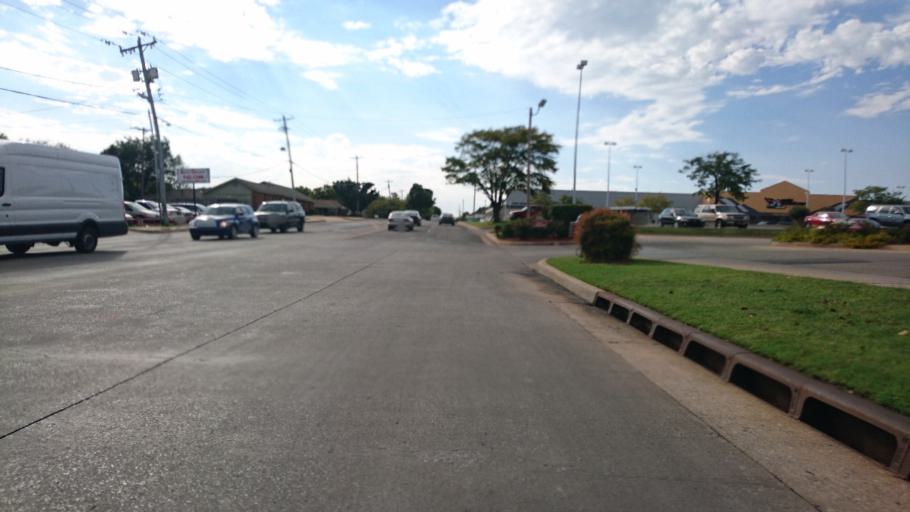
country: US
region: Oklahoma
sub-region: Oklahoma County
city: Nichols Hills
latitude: 35.5077
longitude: -97.5659
